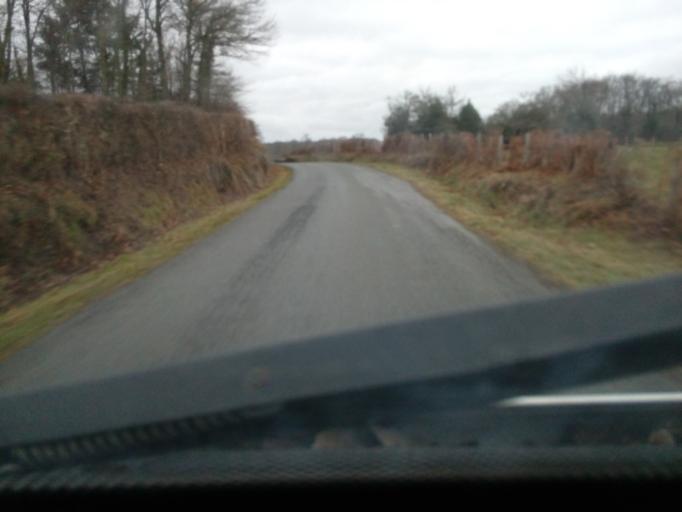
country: FR
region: Limousin
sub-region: Departement de la Creuse
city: Felletin
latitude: 45.8449
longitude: 2.2366
